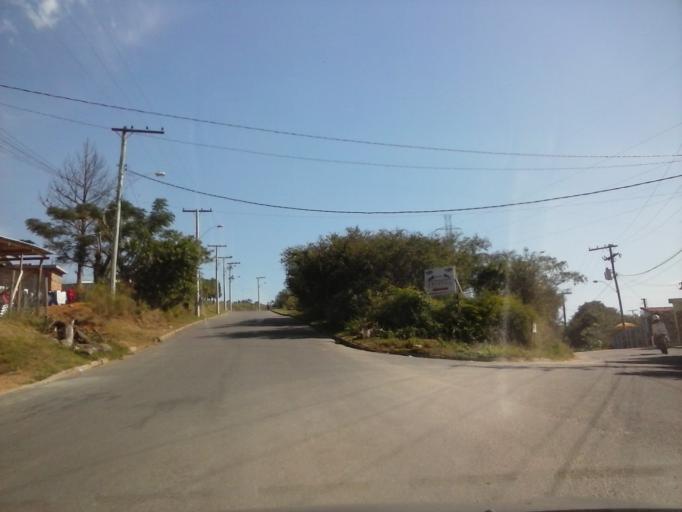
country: BR
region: Rio Grande do Sul
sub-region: Porto Alegre
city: Porto Alegre
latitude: -30.0969
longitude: -51.1787
